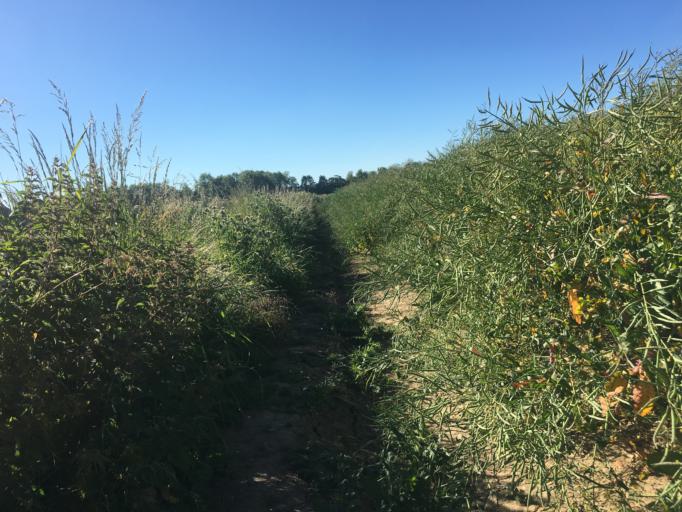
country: GB
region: England
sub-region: Northumberland
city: Beadnell
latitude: 55.5640
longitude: -1.6478
